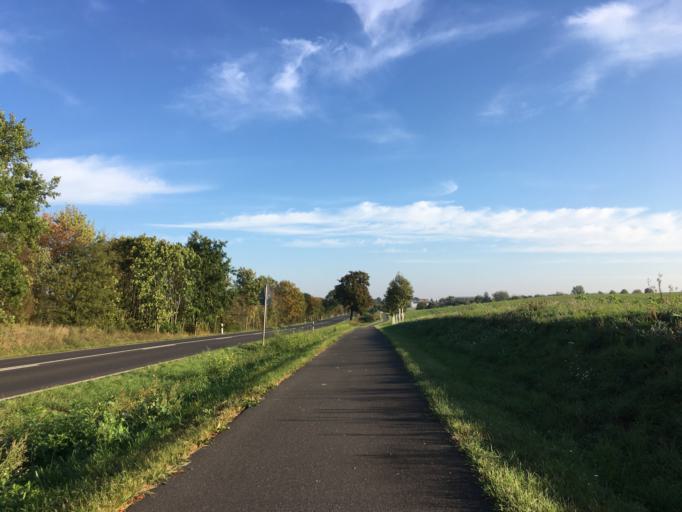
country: DE
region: Brandenburg
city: Lebus
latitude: 52.4115
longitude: 14.5262
